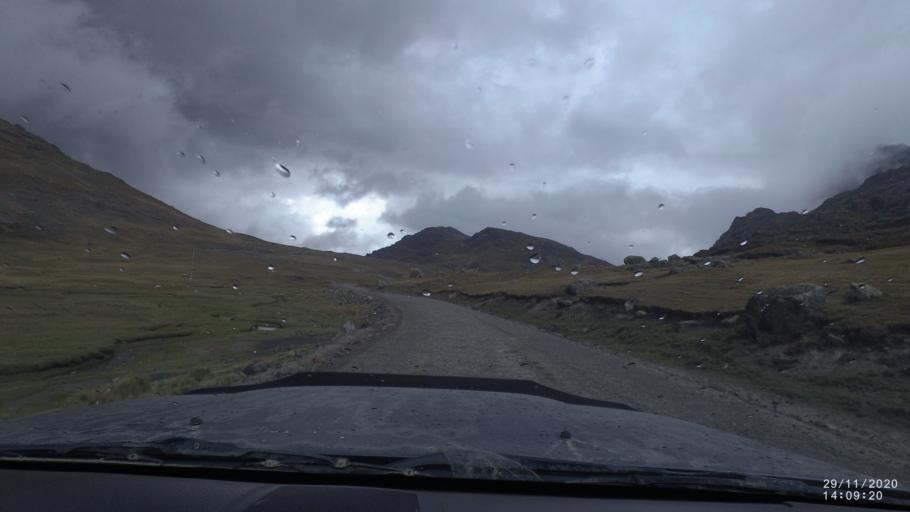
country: BO
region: Cochabamba
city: Sipe Sipe
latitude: -17.2265
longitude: -66.3852
